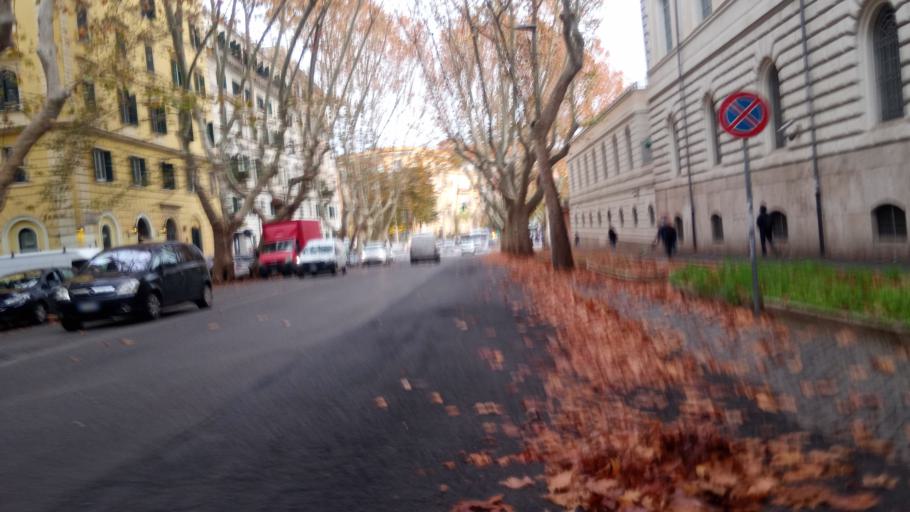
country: IT
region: Latium
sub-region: Citta metropolitana di Roma Capitale
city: Rome
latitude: 41.9019
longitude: 12.5060
